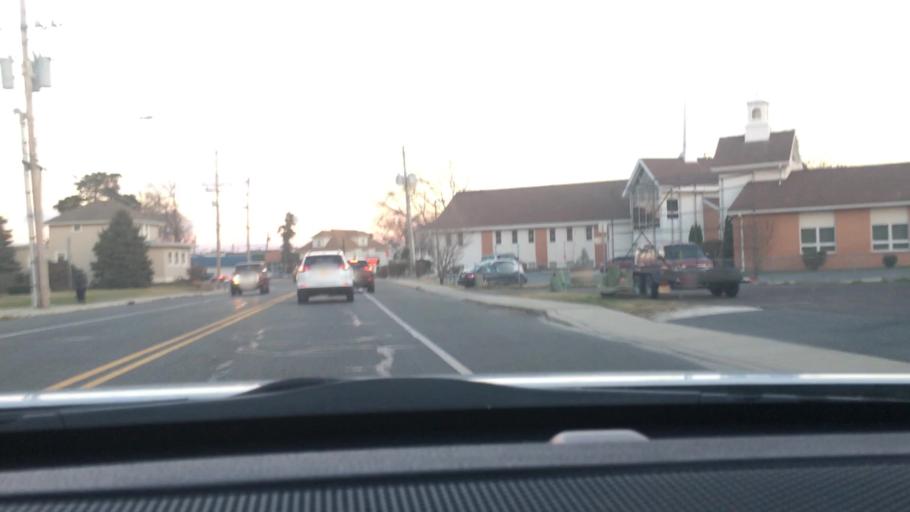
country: US
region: New Jersey
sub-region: Atlantic County
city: Pleasantville
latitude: 39.3906
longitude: -74.5328
